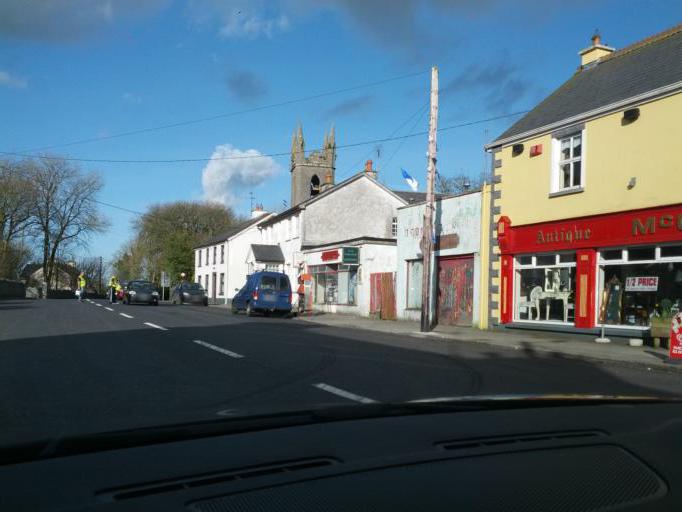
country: IE
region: Connaught
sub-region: Roscommon
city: Castlerea
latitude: 53.6951
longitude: -8.4605
